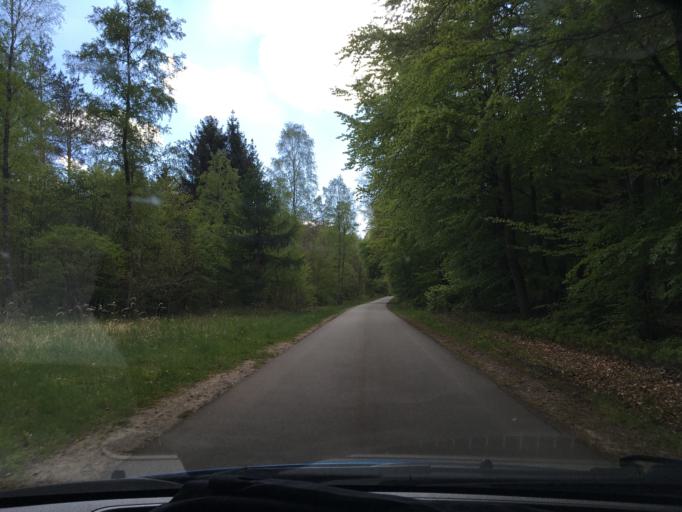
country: DE
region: Lower Saxony
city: Nahrendorf
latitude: 53.1373
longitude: 10.8015
